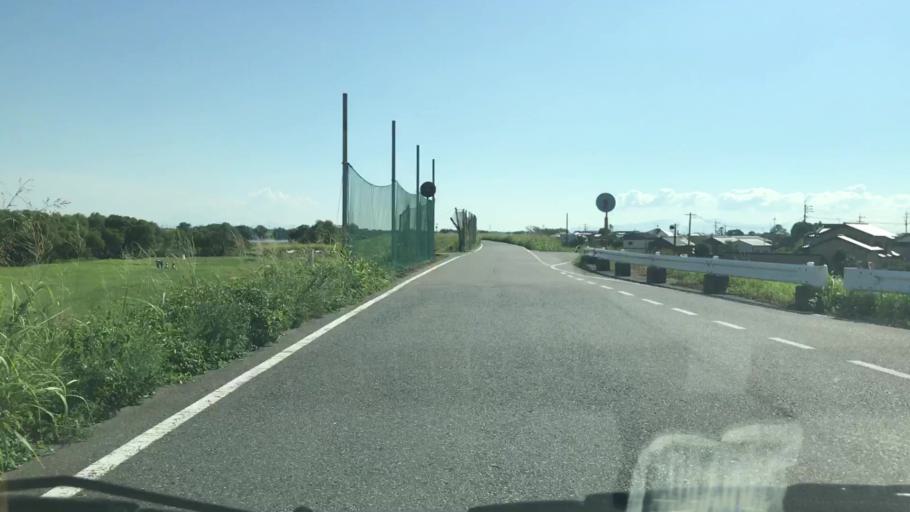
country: JP
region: Fukuoka
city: Kurume
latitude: 33.2822
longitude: 130.4490
